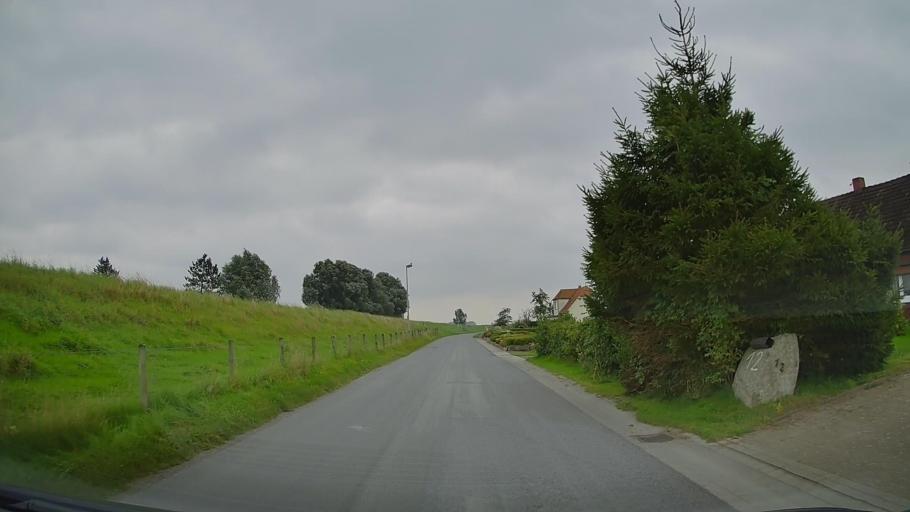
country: DE
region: Lower Saxony
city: Neuhaus an der Oste
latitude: 53.8147
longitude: 9.0327
